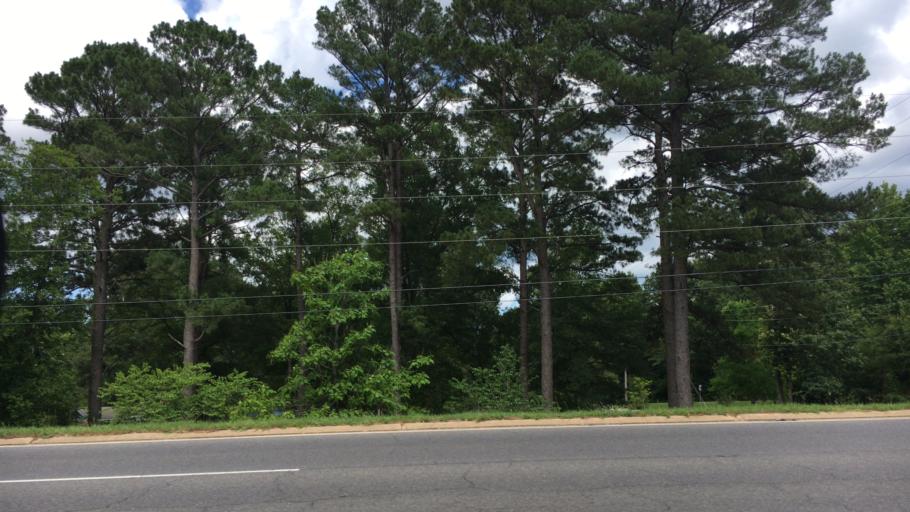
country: US
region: Louisiana
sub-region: Lincoln Parish
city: Ruston
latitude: 32.4969
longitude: -92.6367
